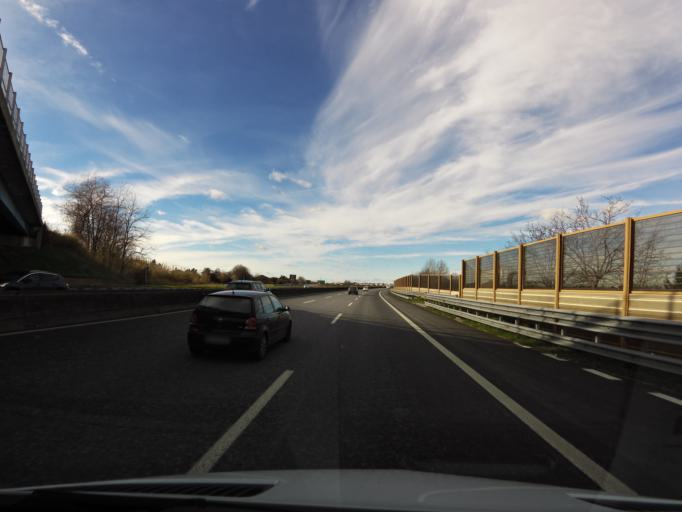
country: IT
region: Emilia-Romagna
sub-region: Forli-Cesena
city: Bagnarola
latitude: 44.1459
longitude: 12.3293
